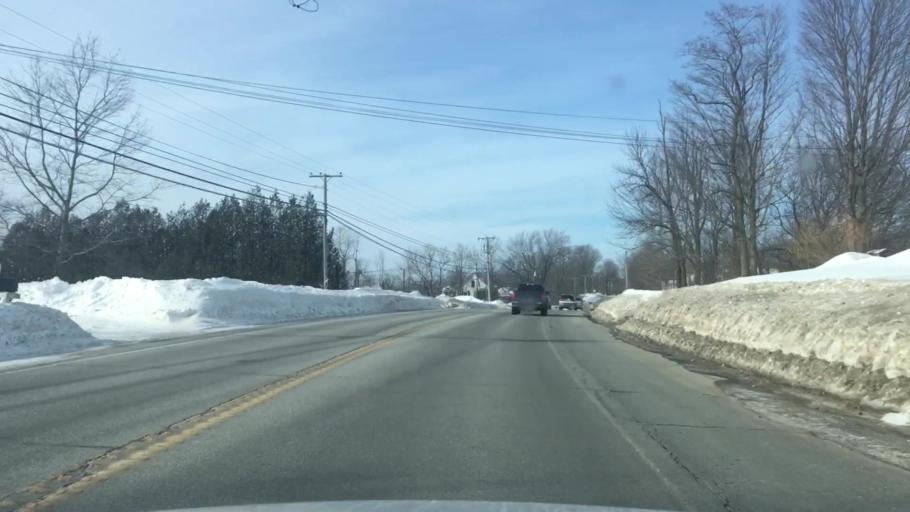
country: US
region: Maine
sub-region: Penobscot County
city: Charleston
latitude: 44.9928
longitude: -69.0184
